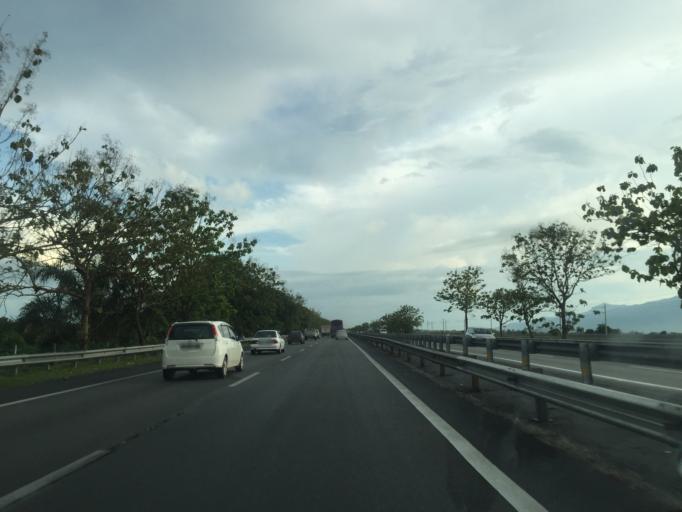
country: MY
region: Kedah
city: Gurun
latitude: 5.9307
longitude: 100.4626
